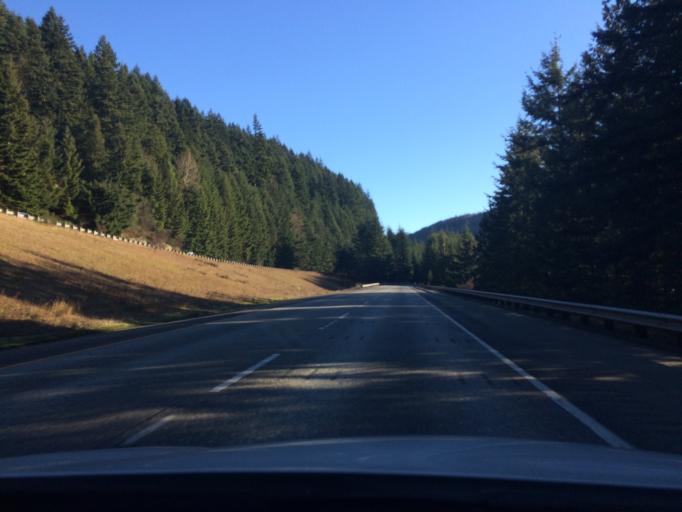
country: US
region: Washington
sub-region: Whatcom County
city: Geneva
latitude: 48.6907
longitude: -122.4326
